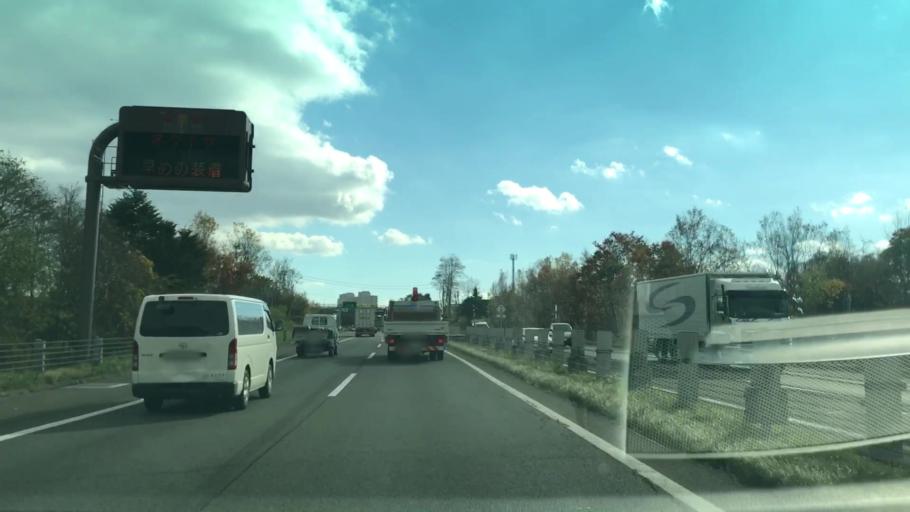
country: JP
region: Hokkaido
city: Kitahiroshima
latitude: 42.9822
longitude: 141.4735
